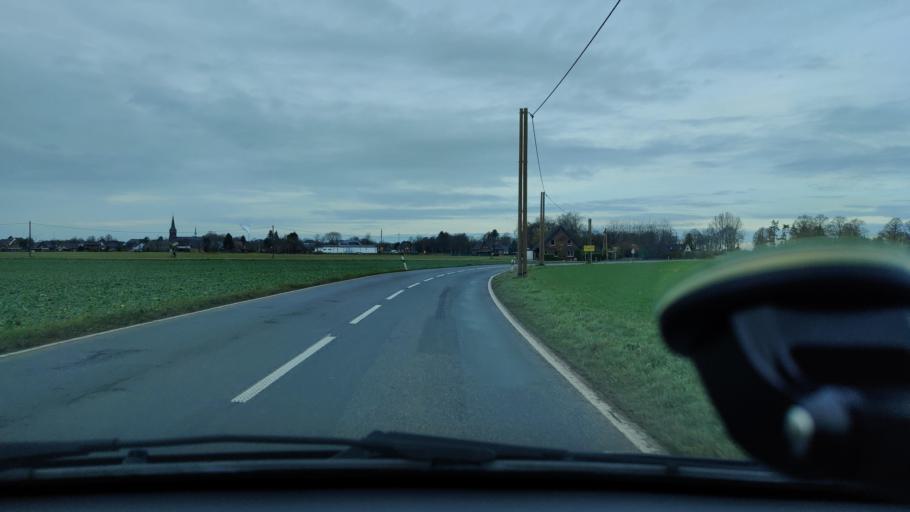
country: DE
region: North Rhine-Westphalia
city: Rees
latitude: 51.6916
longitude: 6.3827
